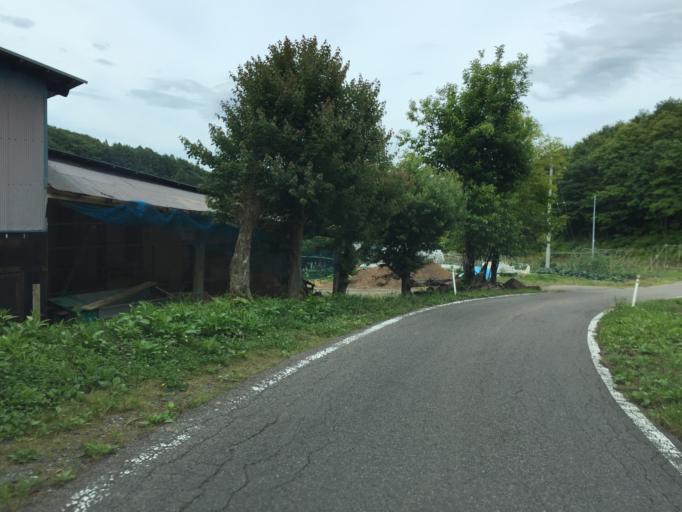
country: JP
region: Fukushima
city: Funehikimachi-funehiki
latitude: 37.4713
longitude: 140.6403
